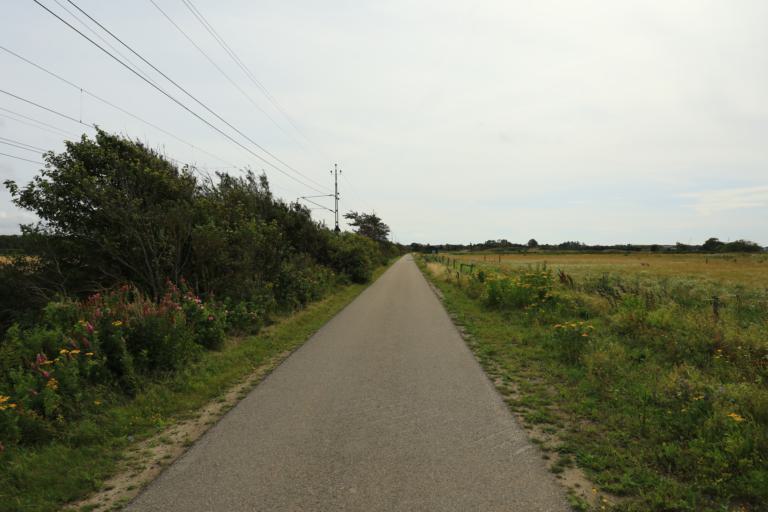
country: SE
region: Halland
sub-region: Varbergs Kommun
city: Varberg
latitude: 57.1370
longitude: 12.2595
